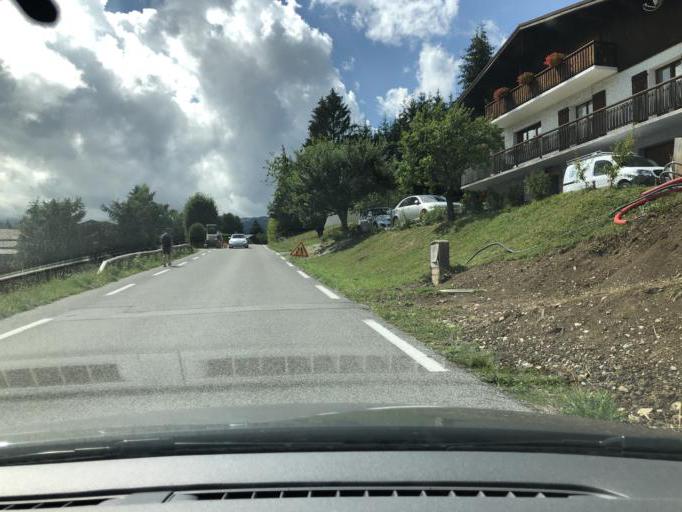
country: FR
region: Rhone-Alpes
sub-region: Departement de la Haute-Savoie
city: Combloux
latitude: 45.8807
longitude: 6.6322
